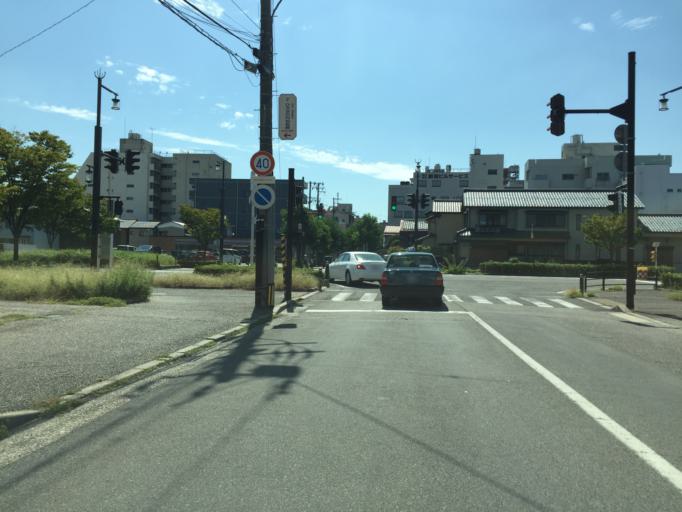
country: JP
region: Niigata
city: Niigata-shi
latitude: 37.9260
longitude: 139.0496
